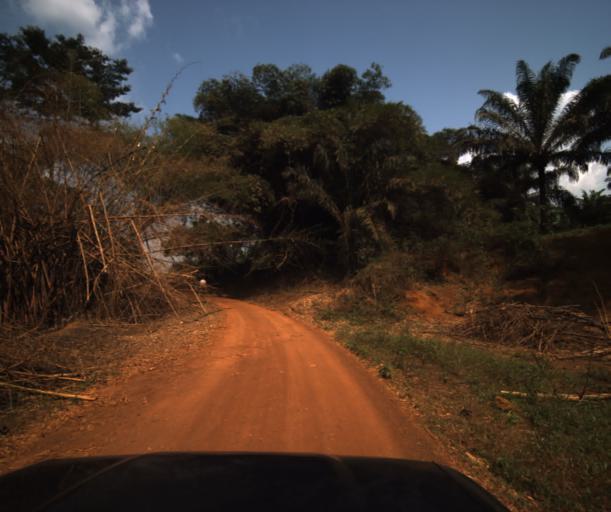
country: CM
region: Centre
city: Akono
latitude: 3.6022
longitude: 11.2361
